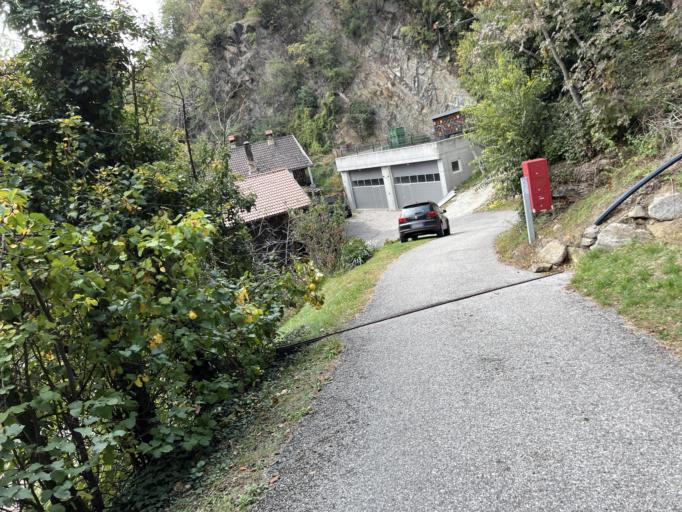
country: IT
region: Trentino-Alto Adige
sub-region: Bolzano
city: Plaus
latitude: 46.6617
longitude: 11.0296
